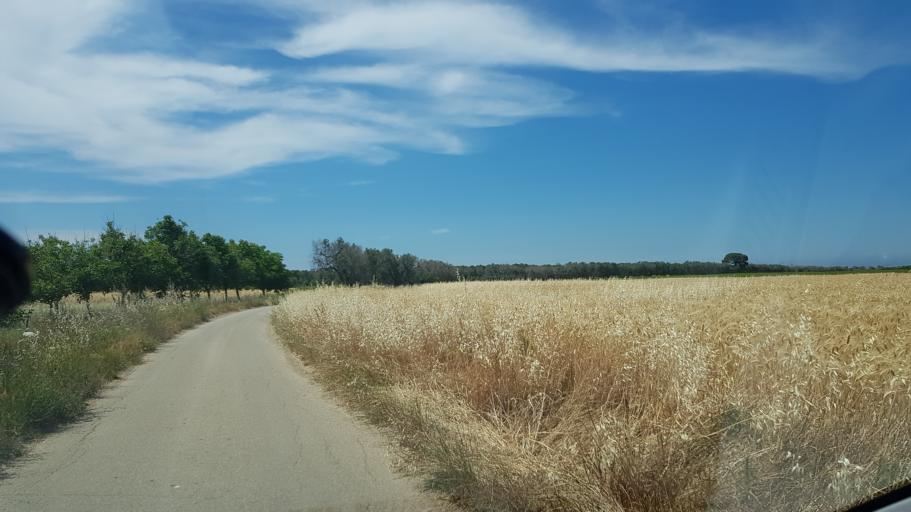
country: IT
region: Apulia
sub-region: Provincia di Brindisi
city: San Pietro Vernotico
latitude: 40.5337
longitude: 17.9972
